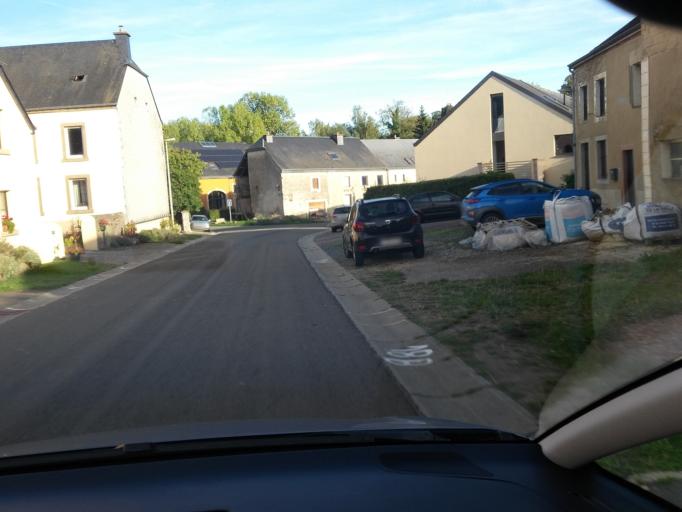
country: BE
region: Wallonia
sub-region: Province du Luxembourg
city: Attert
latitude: 49.7393
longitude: 5.7197
